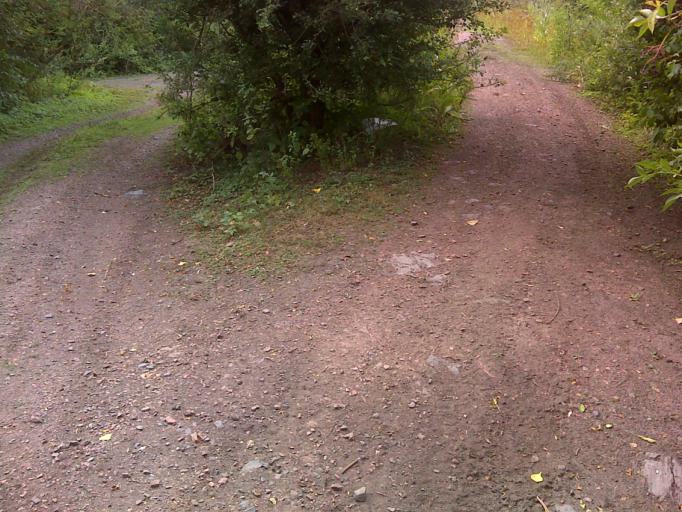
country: FR
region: Nord-Pas-de-Calais
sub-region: Departement du Nord
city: Conde-sur-l'Escaut
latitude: 50.4408
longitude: 3.6004
